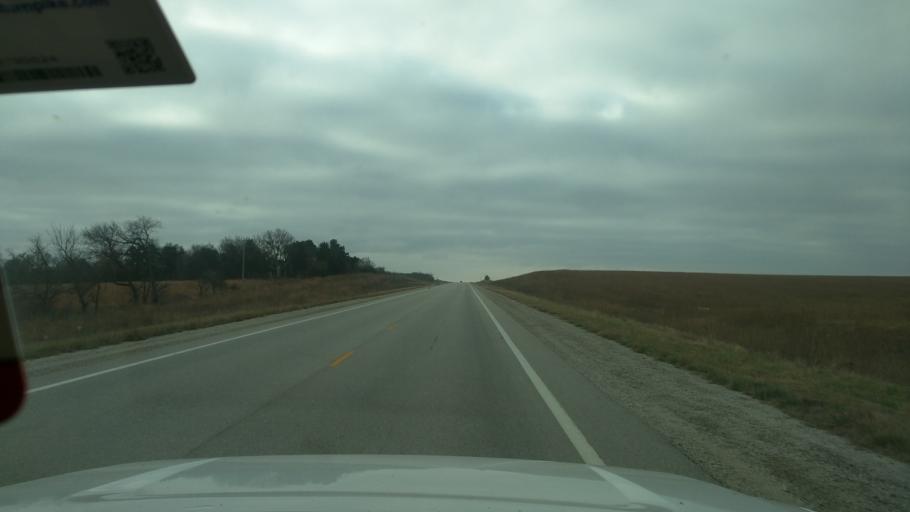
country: US
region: Kansas
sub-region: Elk County
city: Howard
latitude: 37.5881
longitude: -96.2534
